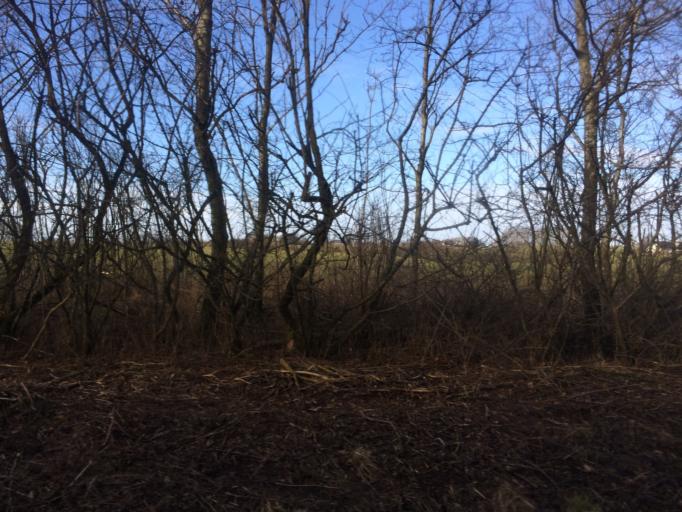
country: DK
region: South Denmark
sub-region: Vejle Kommune
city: Jelling
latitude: 55.7655
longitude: 9.4466
